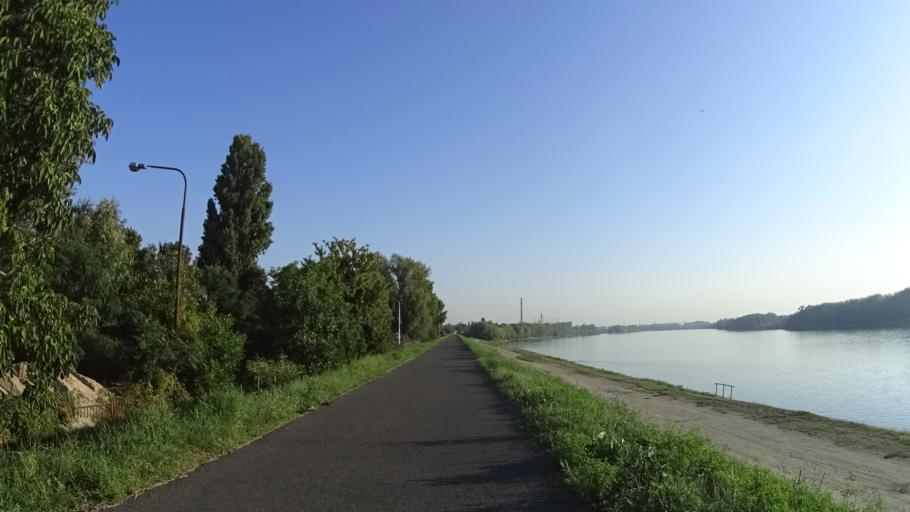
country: HU
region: Budapest
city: Budapest XXII. keruelet
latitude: 47.4427
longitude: 19.0491
